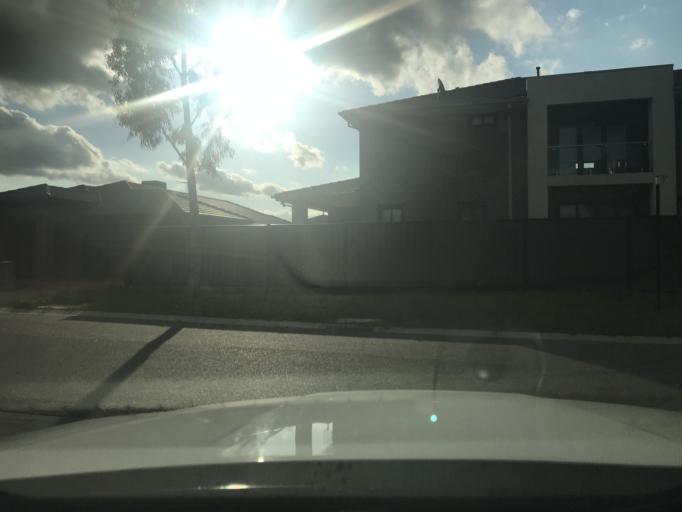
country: AU
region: Victoria
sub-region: Hume
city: Craigieburn
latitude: -37.5749
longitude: 144.9094
